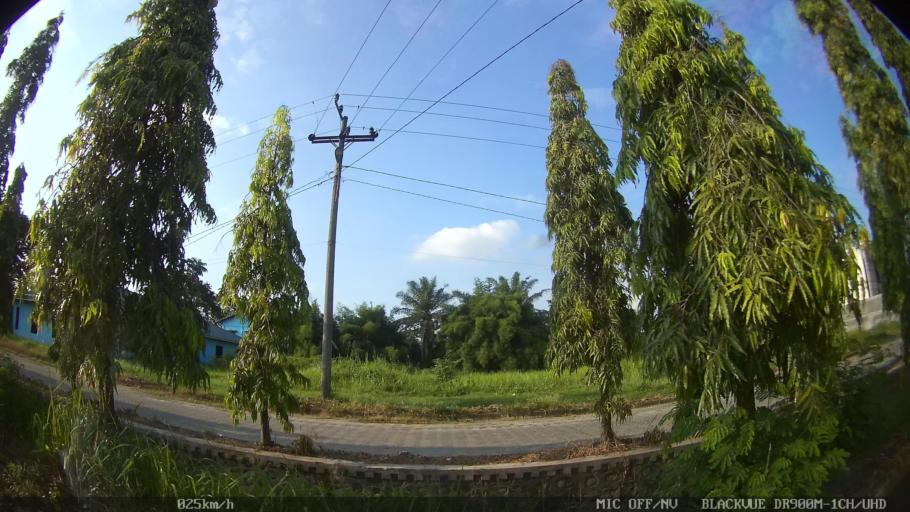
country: ID
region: North Sumatra
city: Medan
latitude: 3.6204
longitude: 98.6438
